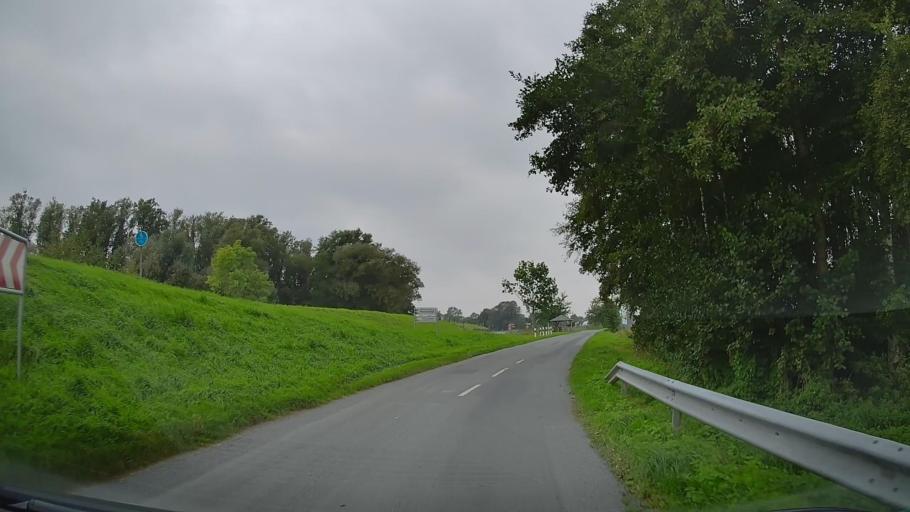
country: DE
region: Lower Saxony
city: Neuhaus an der Oste
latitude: 53.8077
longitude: 9.0332
